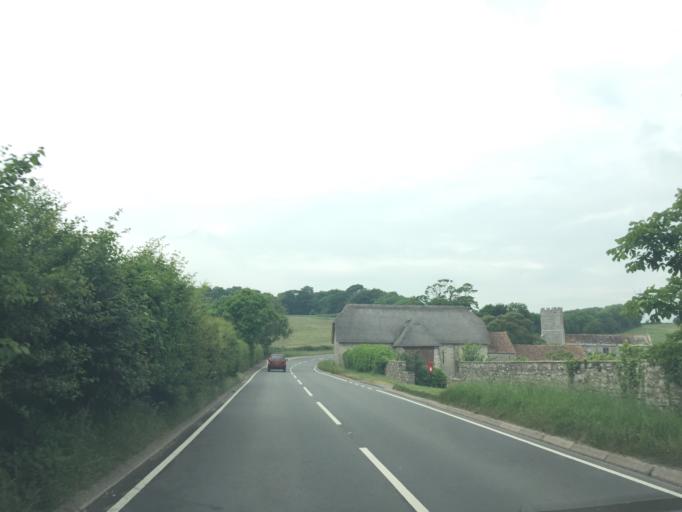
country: GB
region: England
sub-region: Dorset
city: Dorchester
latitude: 50.6923
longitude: -2.4023
